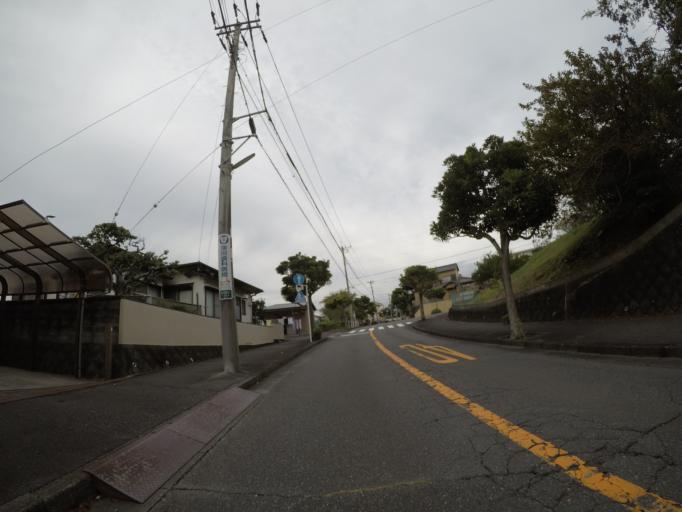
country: JP
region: Shizuoka
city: Fuji
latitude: 35.1836
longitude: 138.7080
